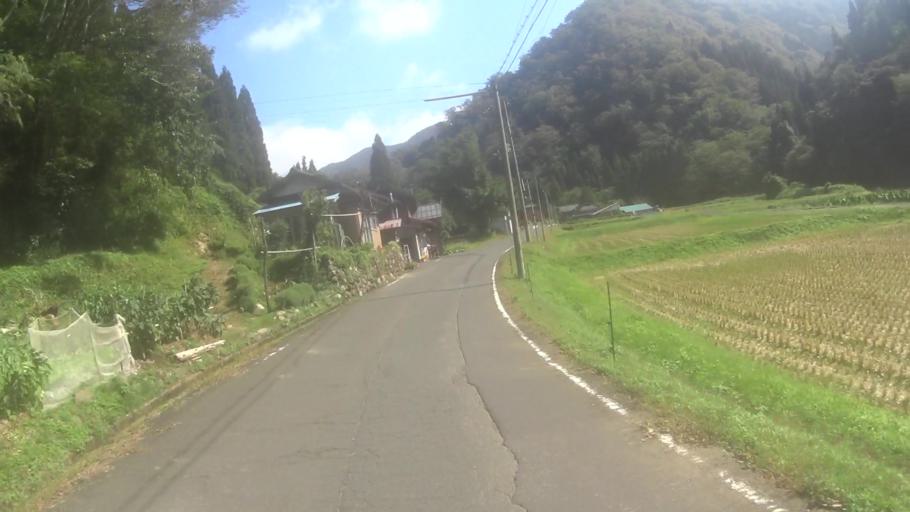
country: JP
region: Kyoto
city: Miyazu
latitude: 35.6811
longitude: 135.1665
